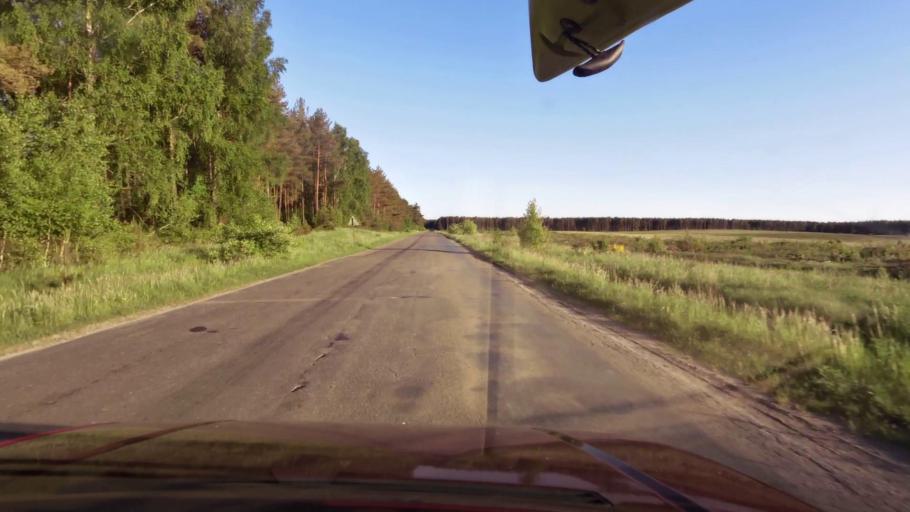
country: PL
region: West Pomeranian Voivodeship
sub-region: Powiat szczecinecki
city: Bialy Bor
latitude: 53.9091
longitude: 16.8101
